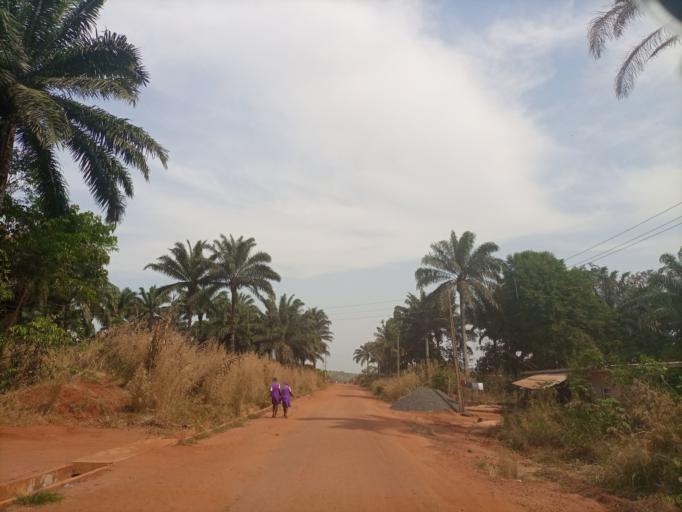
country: NG
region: Enugu
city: Opi
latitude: 6.8222
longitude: 7.4747
